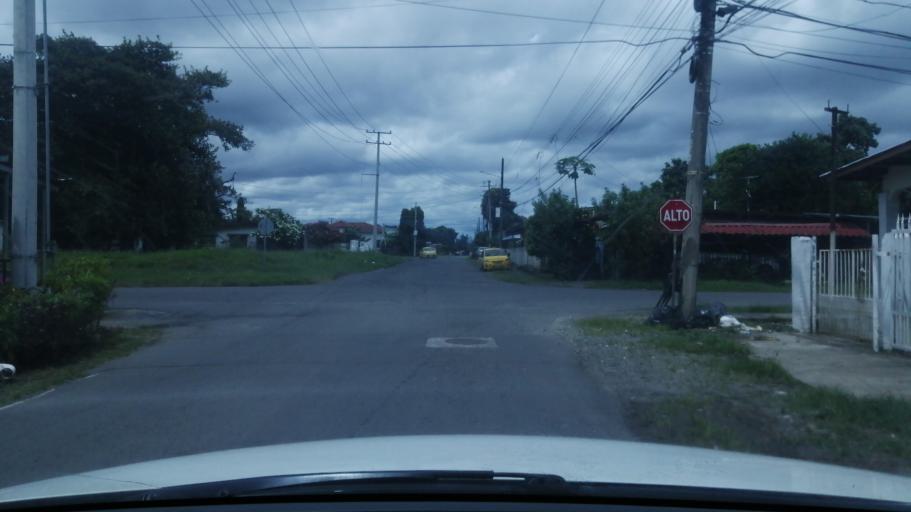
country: PA
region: Chiriqui
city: David
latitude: 8.4293
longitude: -82.4200
